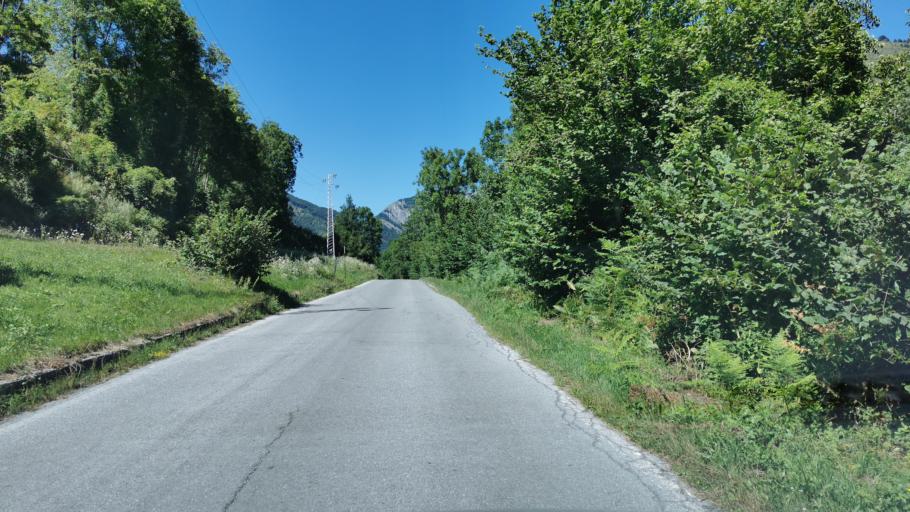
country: IT
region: Piedmont
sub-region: Provincia di Cuneo
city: Entracque
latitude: 44.2405
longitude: 7.3904
